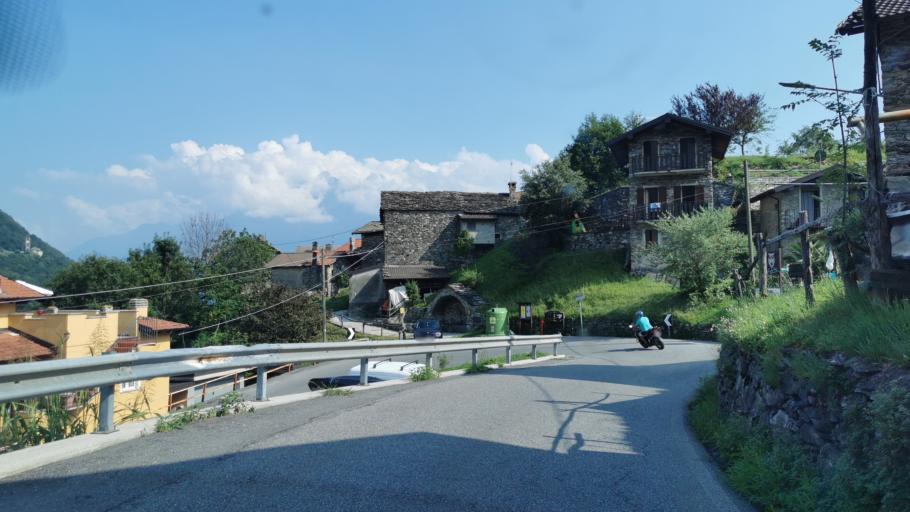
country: IT
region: Lombardy
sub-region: Provincia di Como
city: Dosso del Liro
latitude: 46.1608
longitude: 9.2790
